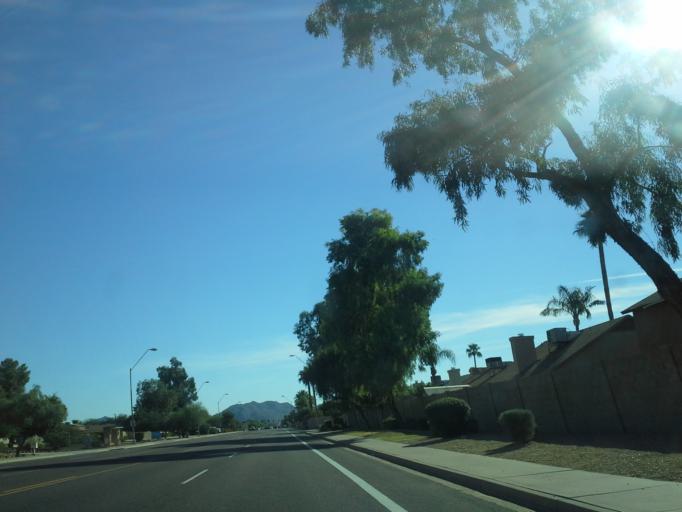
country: US
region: Arizona
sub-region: Maricopa County
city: Paradise Valley
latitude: 33.6310
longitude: -111.9962
